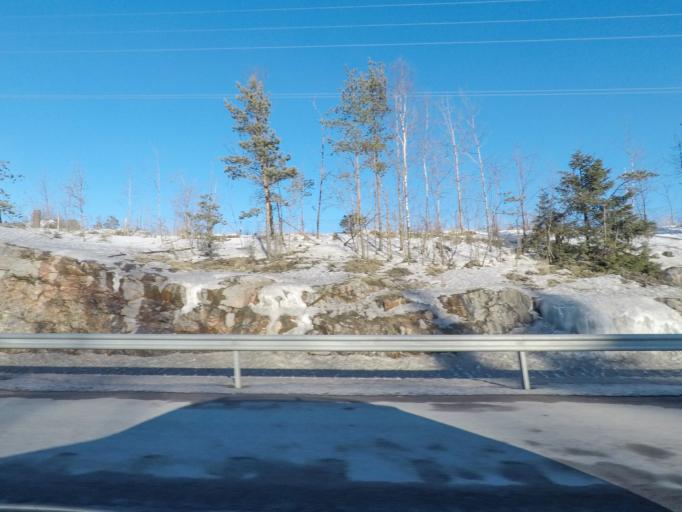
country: FI
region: Uusimaa
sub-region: Helsinki
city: Kerava
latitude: 60.4108
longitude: 25.1265
